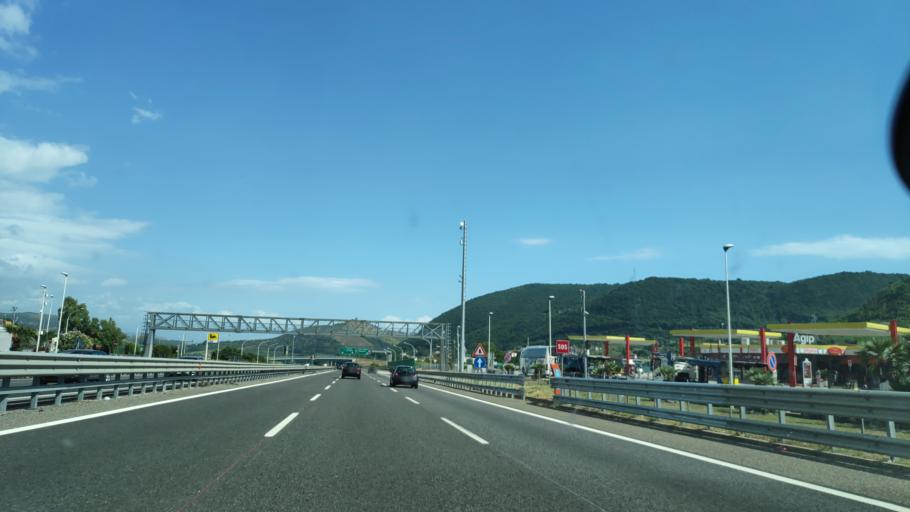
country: IT
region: Campania
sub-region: Provincia di Salerno
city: San Mango Piemonte
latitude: 40.6933
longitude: 14.8342
